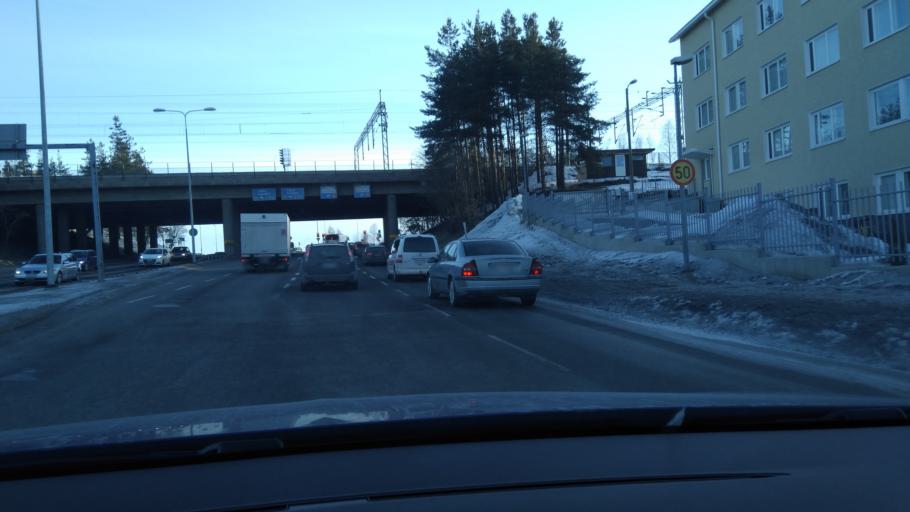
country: FI
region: Pirkanmaa
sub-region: Tampere
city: Pirkkala
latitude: 61.5085
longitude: 23.6881
